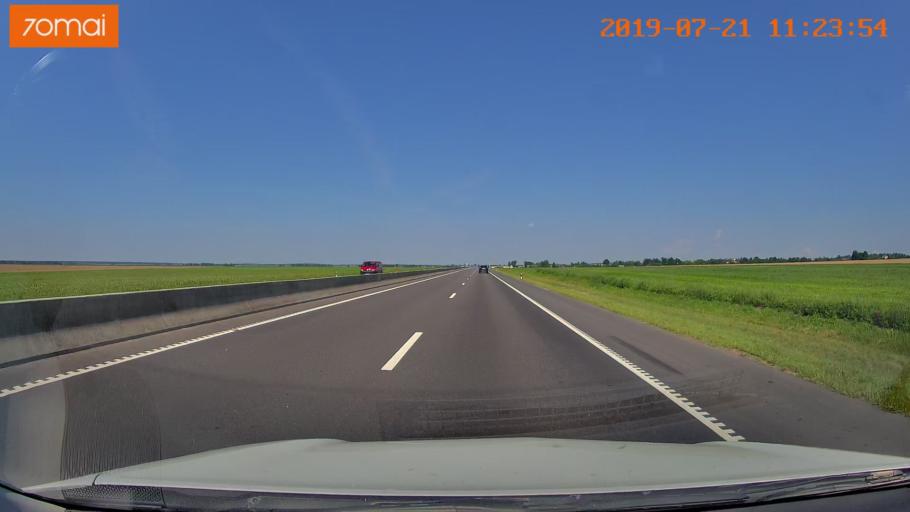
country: BY
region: Minsk
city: Valozhyn
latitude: 54.0512
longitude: 26.5545
